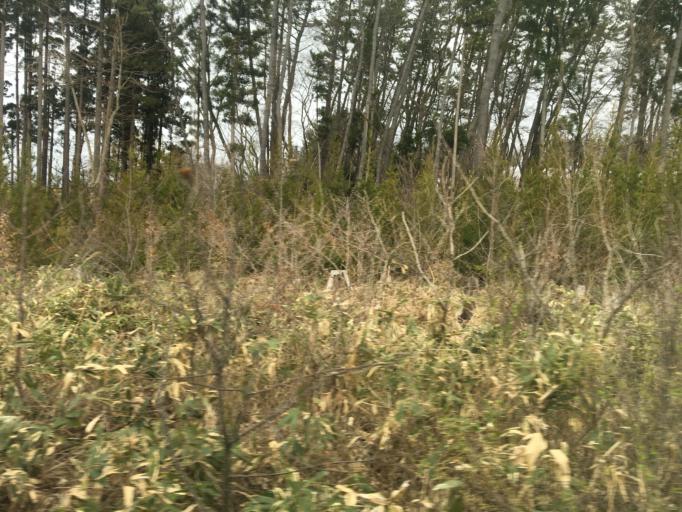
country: JP
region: Aomori
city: Shimokizukuri
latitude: 40.7837
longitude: 140.2838
